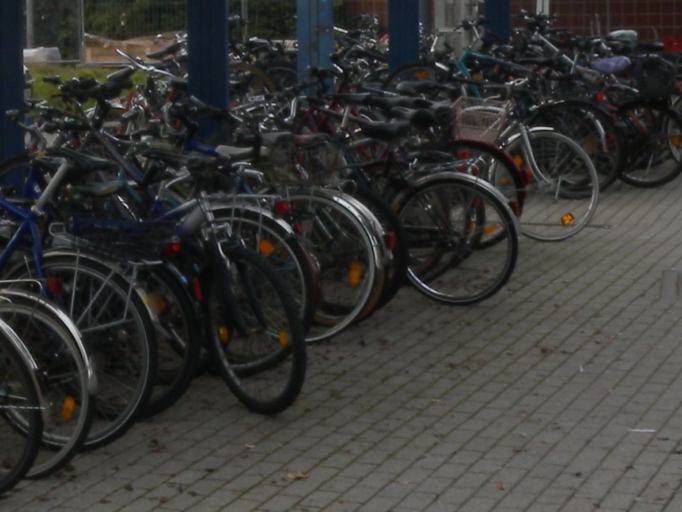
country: DE
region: Baden-Wuerttemberg
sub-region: Karlsruhe Region
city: Buhl
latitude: 48.6970
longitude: 8.1291
